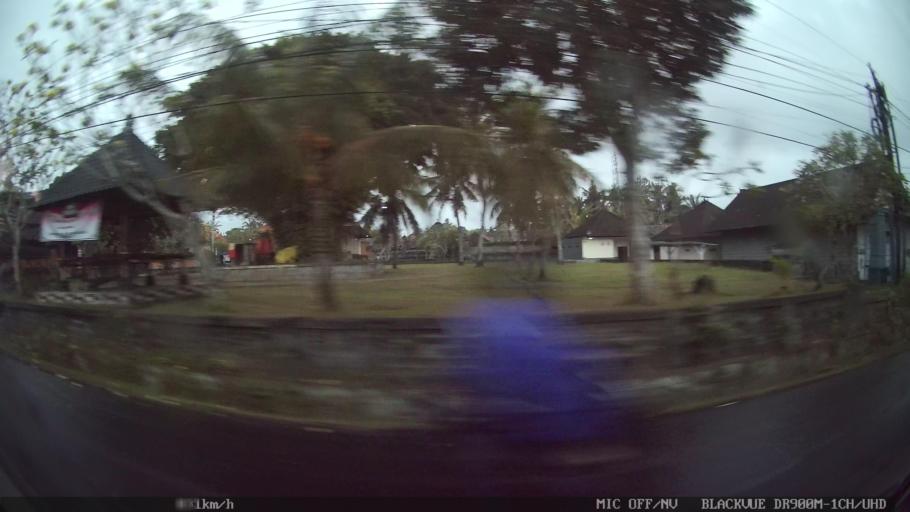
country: ID
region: Bali
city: Banjar Desa
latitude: -8.5833
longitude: 115.2677
